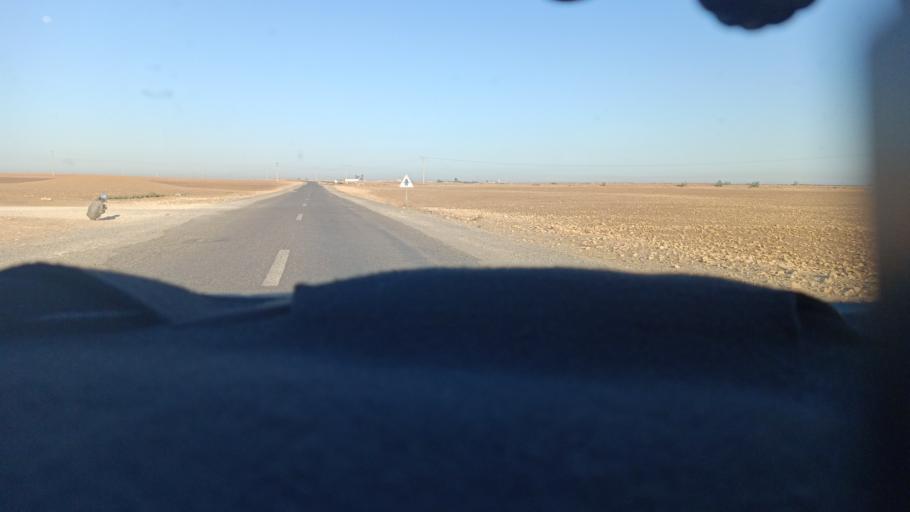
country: MA
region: Doukkala-Abda
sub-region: Safi
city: Youssoufia
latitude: 32.3697
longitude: -8.6275
